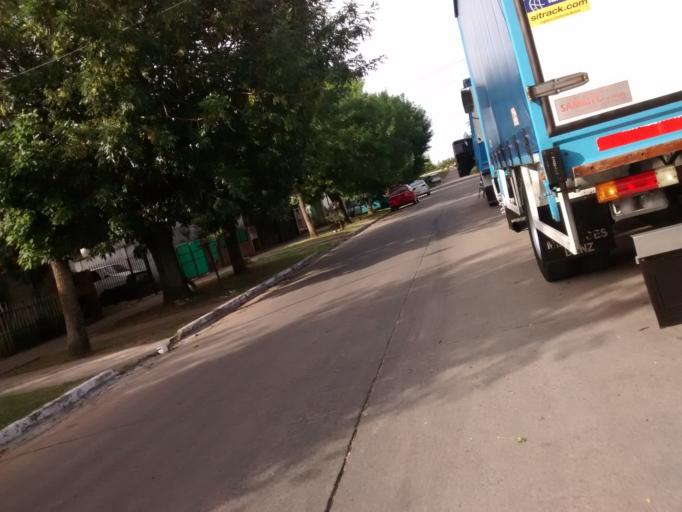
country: AR
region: Buenos Aires
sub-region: Partido de La Plata
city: La Plata
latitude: -34.8525
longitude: -58.0723
